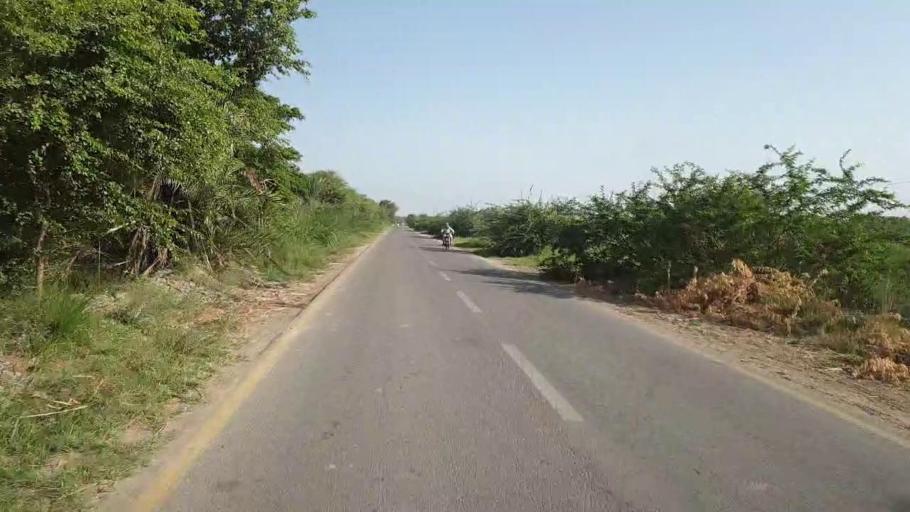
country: PK
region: Sindh
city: Daur
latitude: 26.4579
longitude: 68.4507
